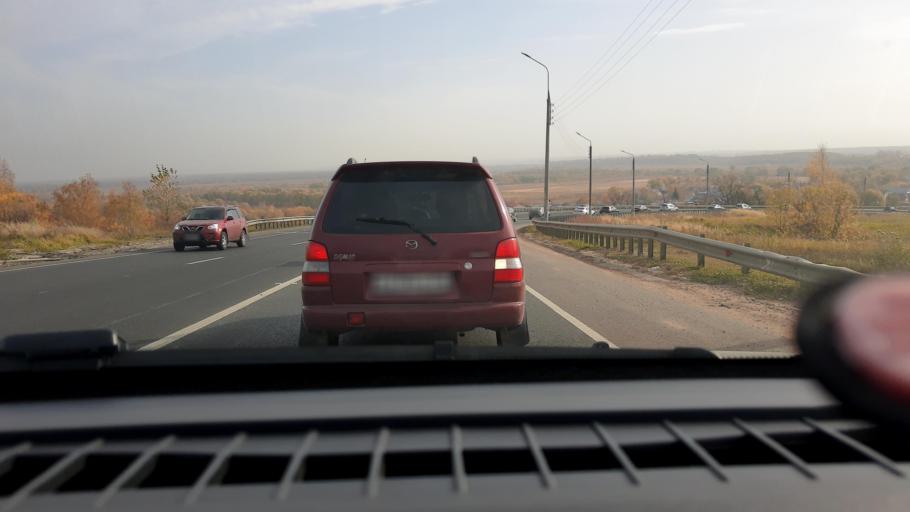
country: RU
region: Nizjnij Novgorod
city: Afonino
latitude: 56.2418
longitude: 44.1021
